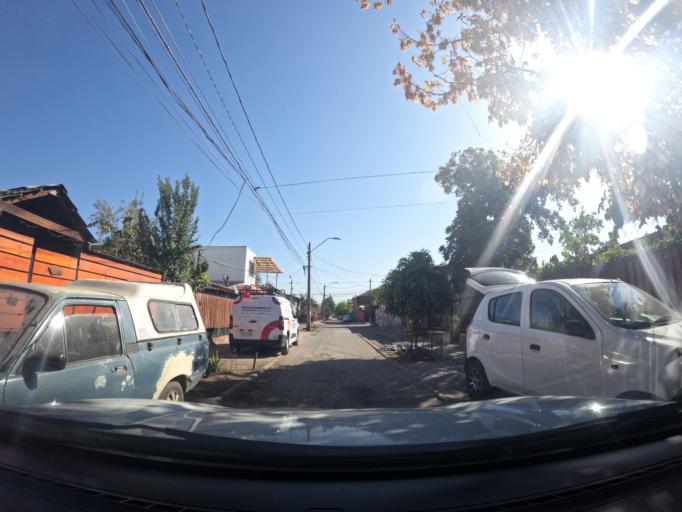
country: CL
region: Santiago Metropolitan
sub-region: Provincia de Santiago
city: Villa Presidente Frei, Nunoa, Santiago, Chile
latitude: -33.4785
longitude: -70.5771
